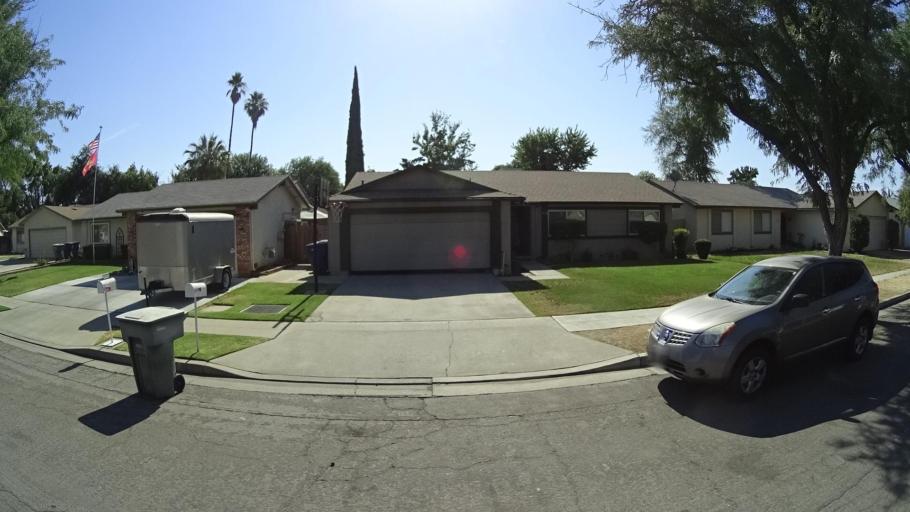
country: US
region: California
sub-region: Fresno County
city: Tarpey Village
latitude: 36.7858
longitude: -119.6889
